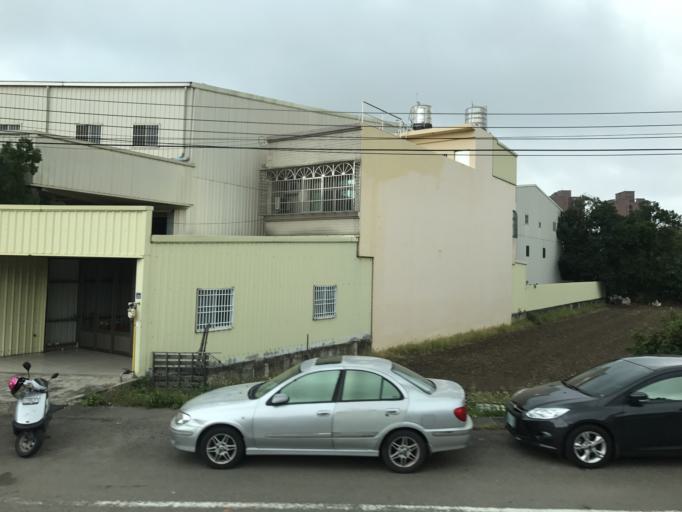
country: TW
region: Taiwan
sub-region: Hsinchu
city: Hsinchu
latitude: 24.8171
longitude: 120.9566
